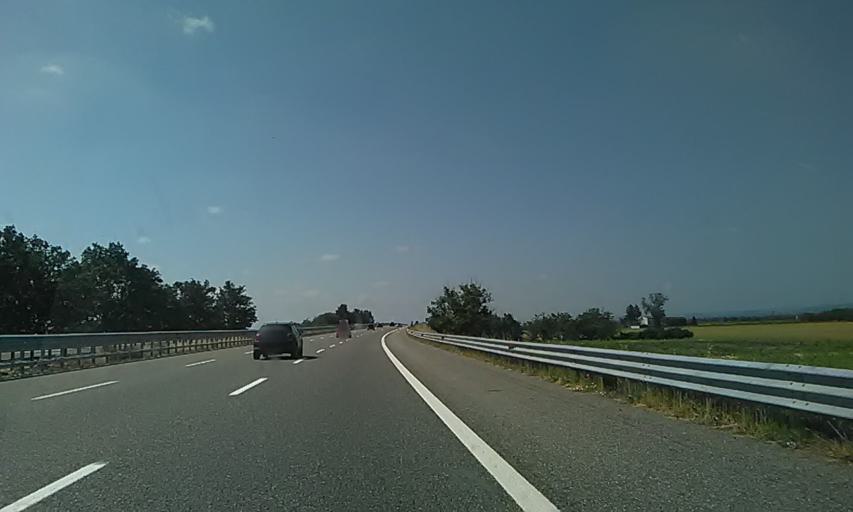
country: IT
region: Piedmont
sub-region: Provincia di Alessandria
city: Castellazzo Bormida
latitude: 44.8375
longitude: 8.5963
